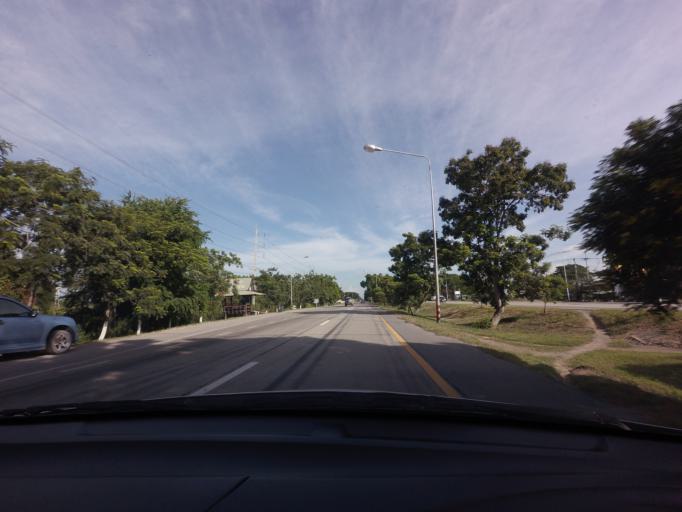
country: TH
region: Suphan Buri
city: Bang Pla Ma
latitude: 14.3818
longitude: 100.1772
